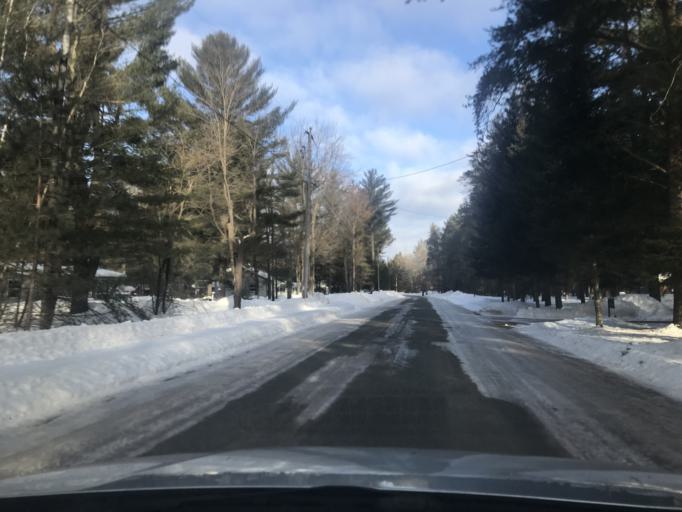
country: US
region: Wisconsin
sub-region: Marinette County
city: Niagara
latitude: 45.6338
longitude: -87.9683
